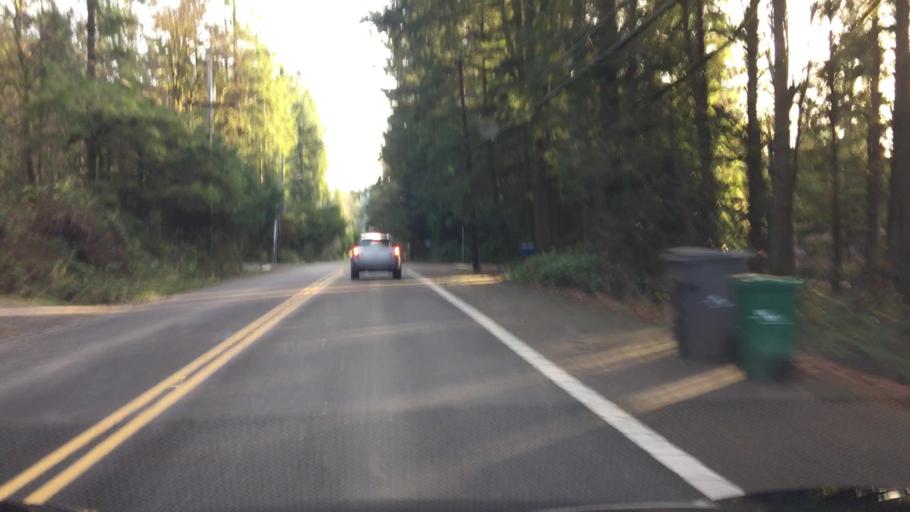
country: US
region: Washington
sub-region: King County
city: Woodinville
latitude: 47.7717
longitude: -122.1318
